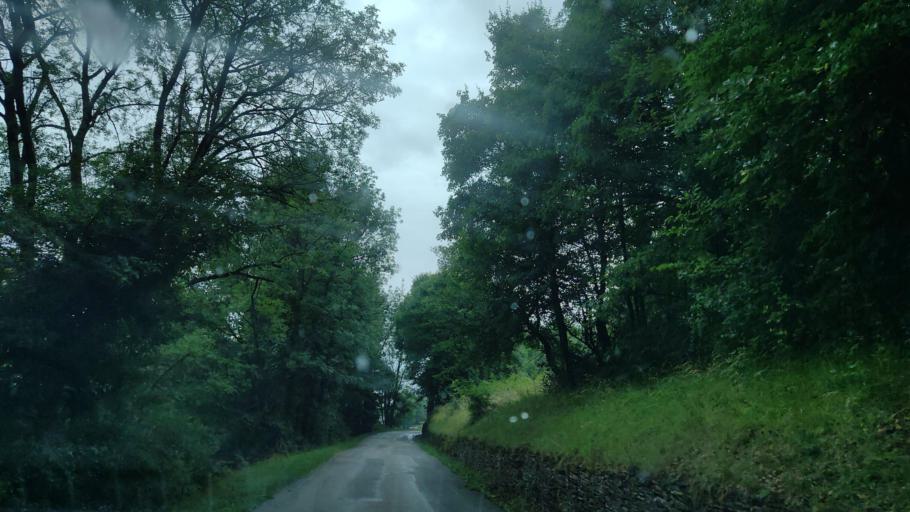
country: FR
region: Rhone-Alpes
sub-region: Departement de la Savoie
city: Coise-Saint-Jean-Pied-Gauthier
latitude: 45.5092
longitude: 6.1529
